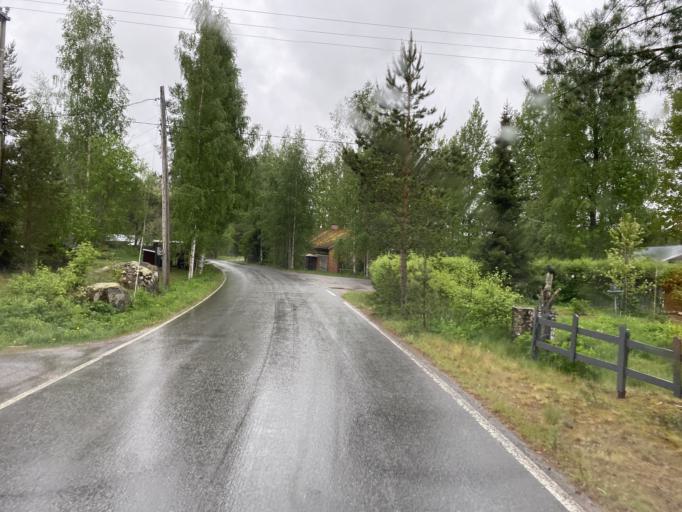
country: FI
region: Haeme
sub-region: Forssa
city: Humppila
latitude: 61.0674
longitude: 23.3195
